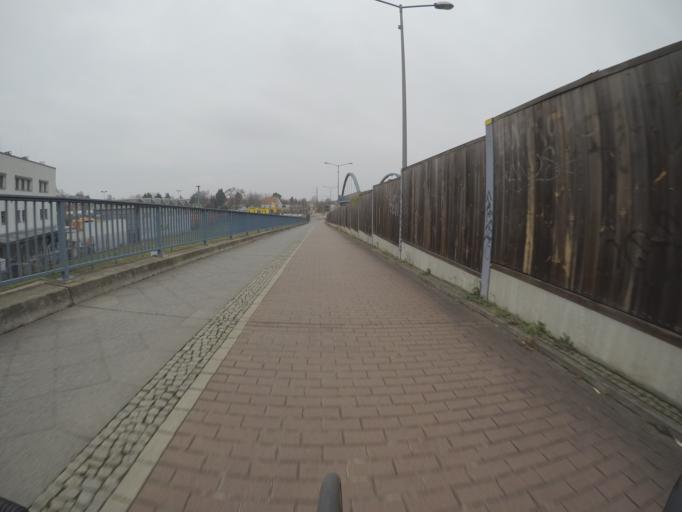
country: DE
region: Berlin
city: Kopenick Bezirk
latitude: 52.4475
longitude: 13.5594
